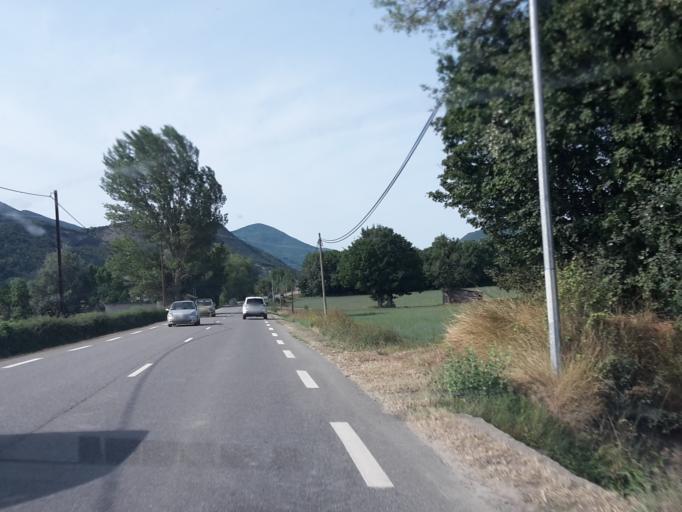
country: FR
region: Provence-Alpes-Cote d'Azur
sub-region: Departement des Hautes-Alpes
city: La Batie-Neuve
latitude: 44.5478
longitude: 6.2000
